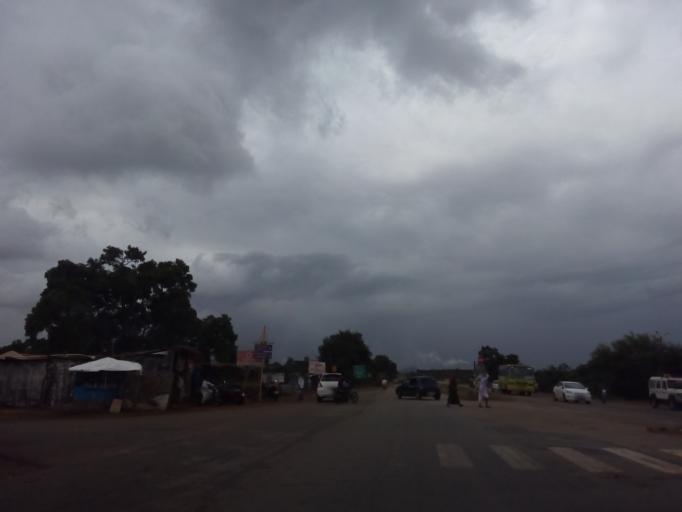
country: IN
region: Karnataka
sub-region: Davanagere
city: Harihar
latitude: 14.5372
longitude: 75.7618
